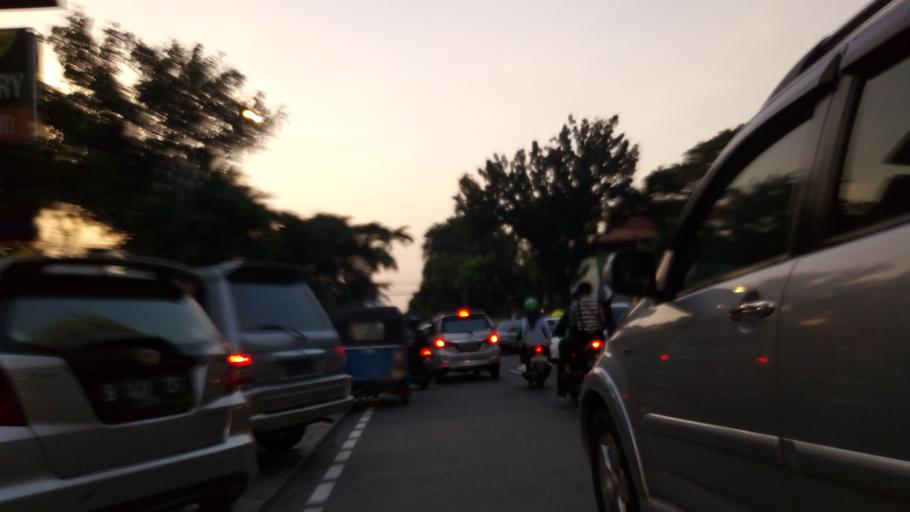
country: ID
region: Jakarta Raya
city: Jakarta
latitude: -6.2442
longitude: 106.7971
